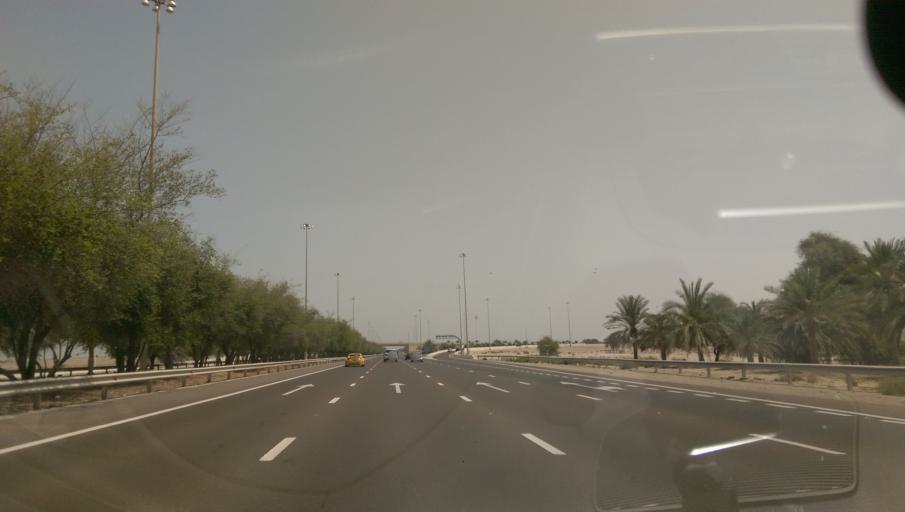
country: AE
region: Abu Dhabi
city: Abu Dhabi
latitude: 24.4599
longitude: 54.6779
